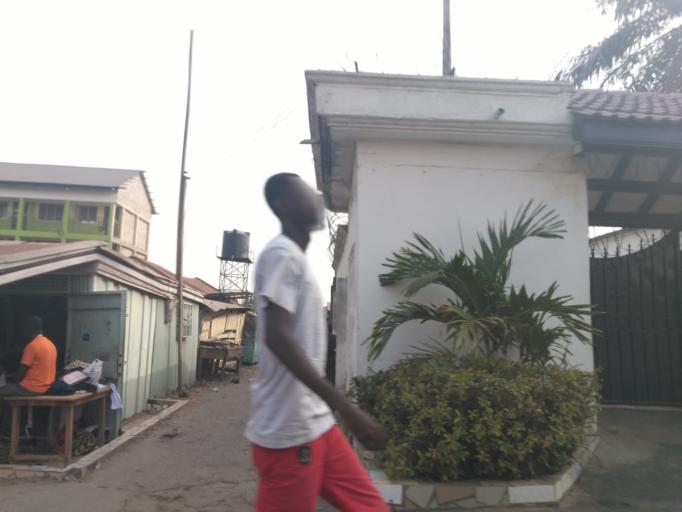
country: GH
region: Ashanti
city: Kumasi
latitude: 6.6883
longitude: -1.6091
